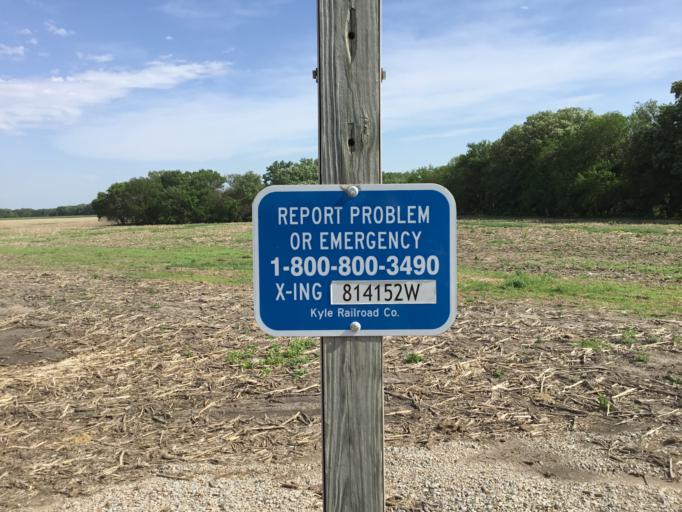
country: US
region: Kansas
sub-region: Mitchell County
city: Beloit
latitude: 39.4081
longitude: -97.9828
